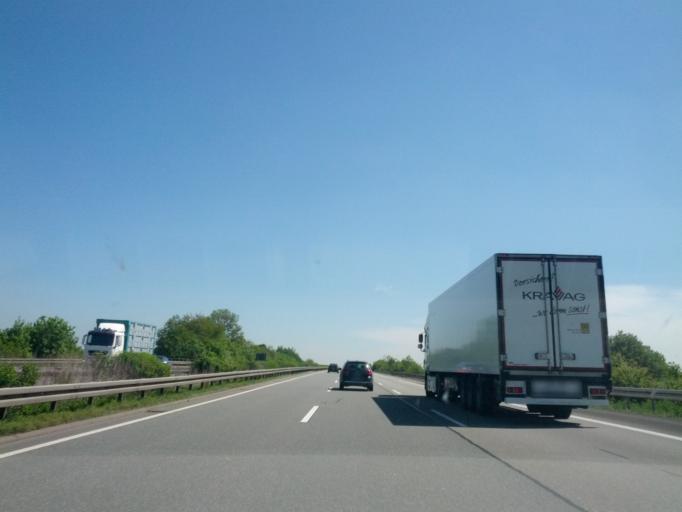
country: DE
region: Thuringia
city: Emleben
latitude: 50.9012
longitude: 10.6991
